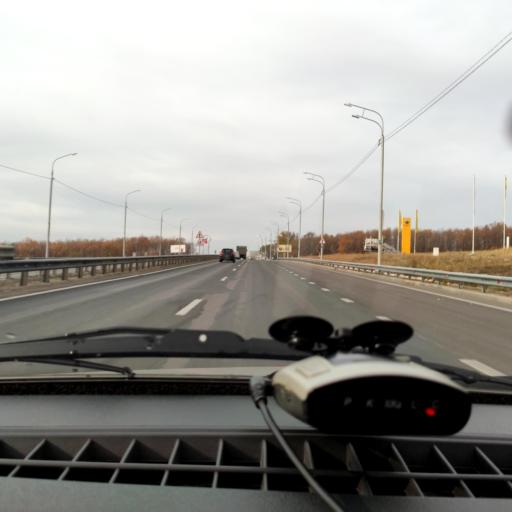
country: RU
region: Voronezj
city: Pridonskoy
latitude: 51.6518
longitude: 39.0517
